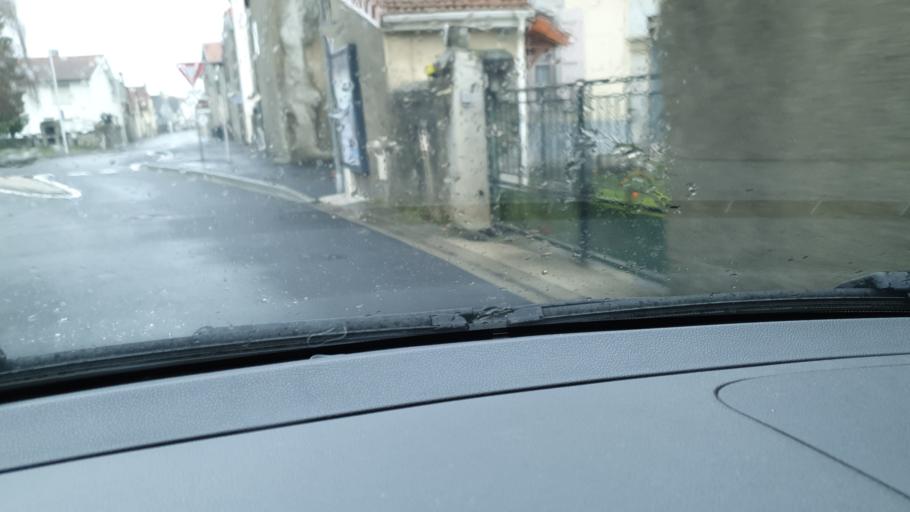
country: FR
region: Midi-Pyrenees
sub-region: Departement des Hautes-Pyrenees
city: Tarbes
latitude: 43.2530
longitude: 0.0537
